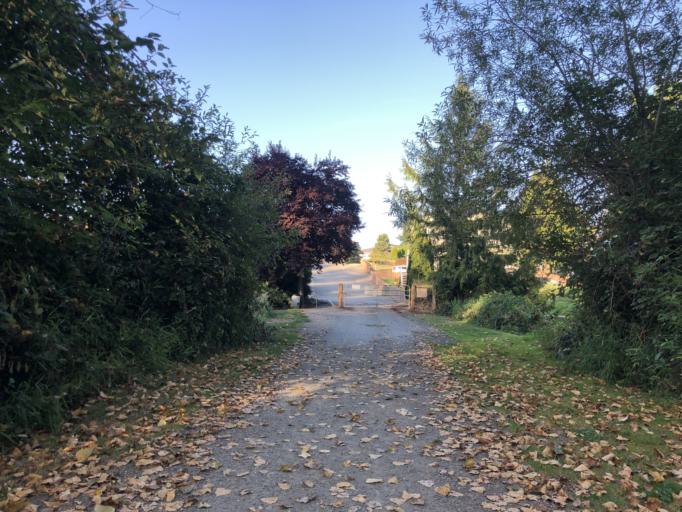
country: US
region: Washington
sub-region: Pierce County
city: Bonney Lake
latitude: 47.2243
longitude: -122.1684
